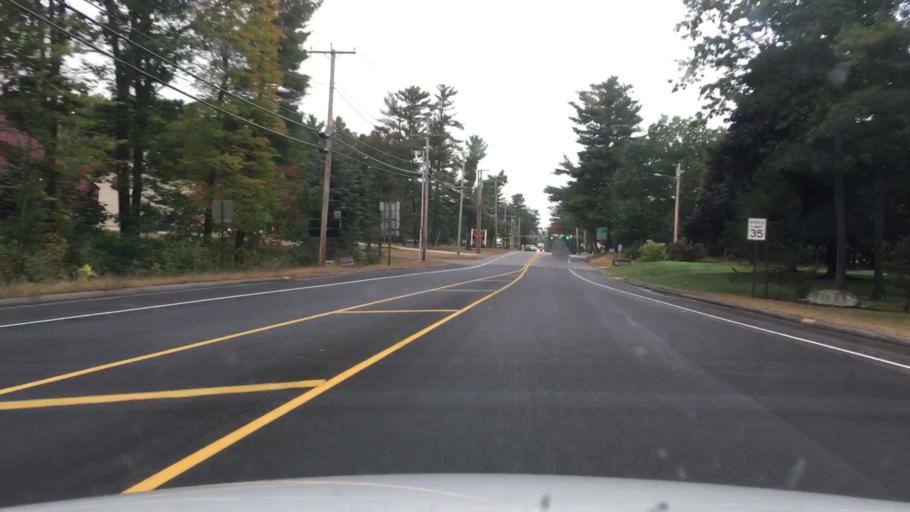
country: US
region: Maine
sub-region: Cumberland County
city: New Gloucester
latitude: 43.9001
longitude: -70.3437
